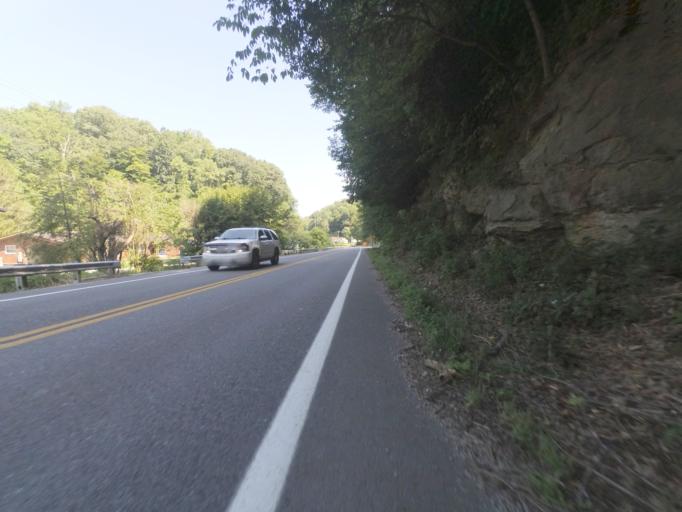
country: US
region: West Virginia
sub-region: Cabell County
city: Huntington
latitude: 38.3744
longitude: -82.4548
